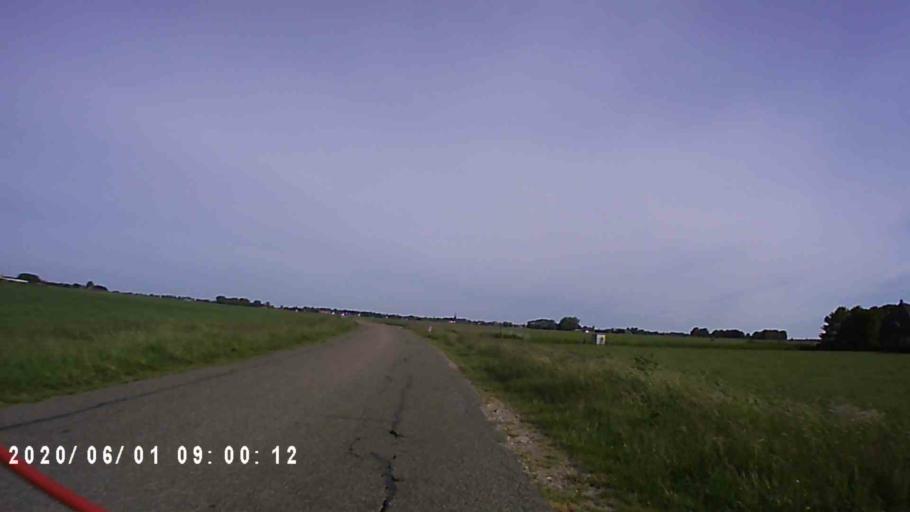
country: NL
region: Friesland
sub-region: Gemeente Ferwerderadiel
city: Hallum
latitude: 53.2858
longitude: 5.7972
